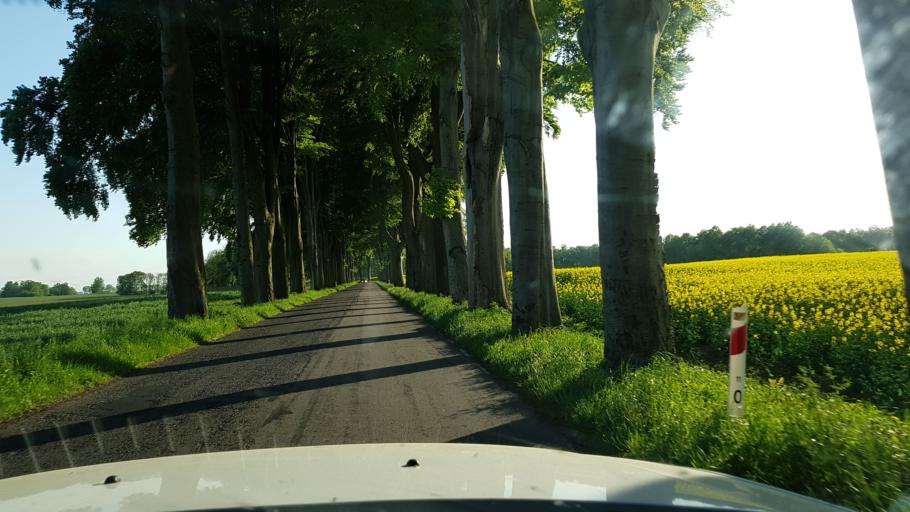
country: PL
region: West Pomeranian Voivodeship
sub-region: Powiat lobeski
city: Dobra
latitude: 53.5834
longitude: 15.2815
